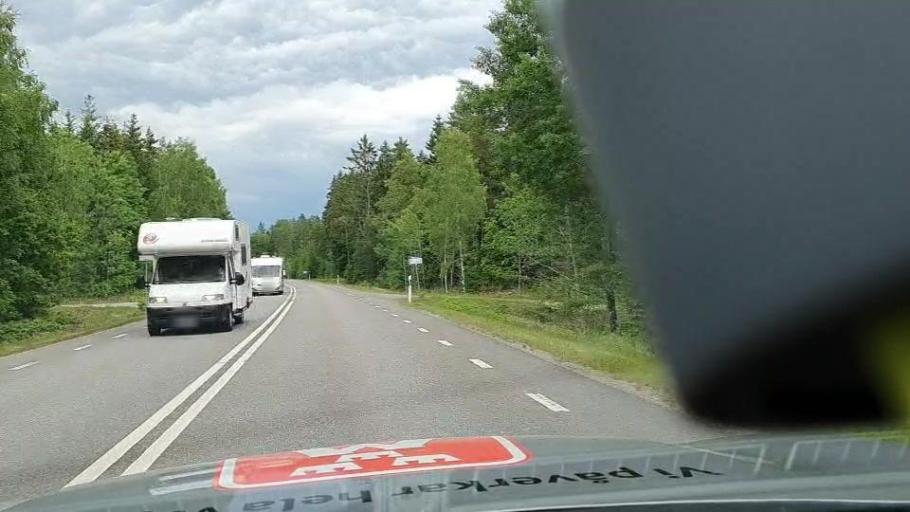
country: SE
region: Kalmar
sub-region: Emmaboda Kommun
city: Emmaboda
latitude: 56.4545
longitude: 15.5814
